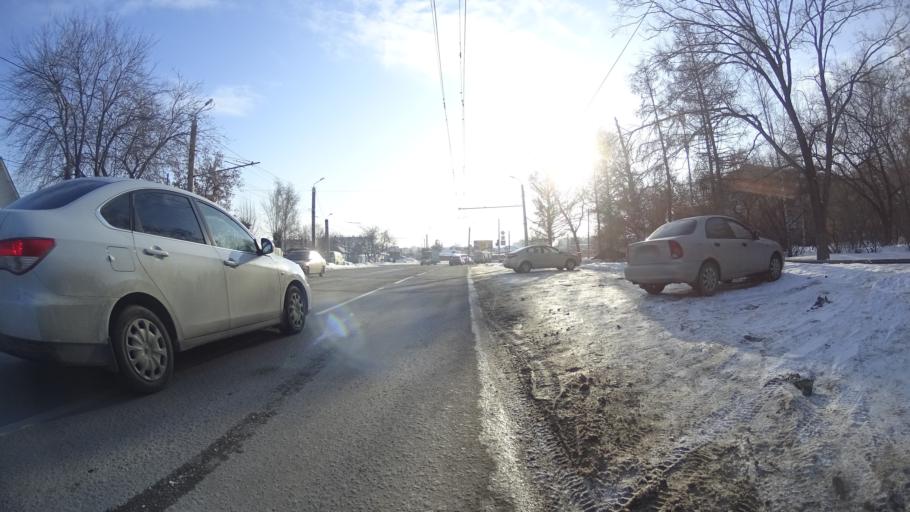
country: RU
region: Chelyabinsk
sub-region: Gorod Chelyabinsk
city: Chelyabinsk
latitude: 55.1846
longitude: 61.4590
